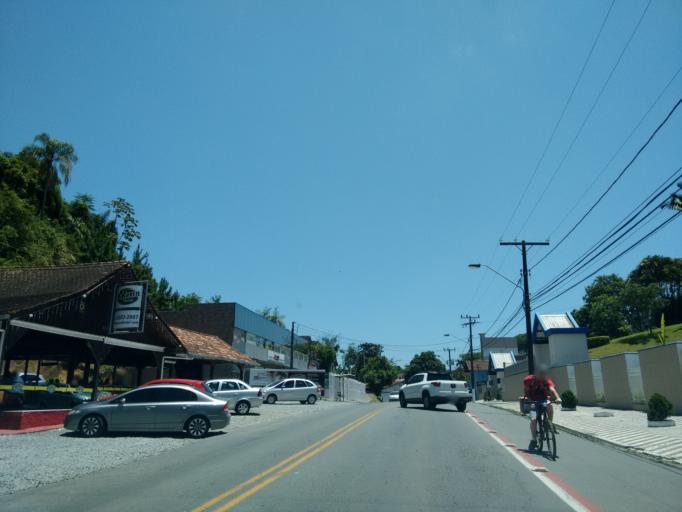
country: BR
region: Santa Catarina
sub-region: Blumenau
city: Blumenau
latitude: -26.8806
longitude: -49.0775
